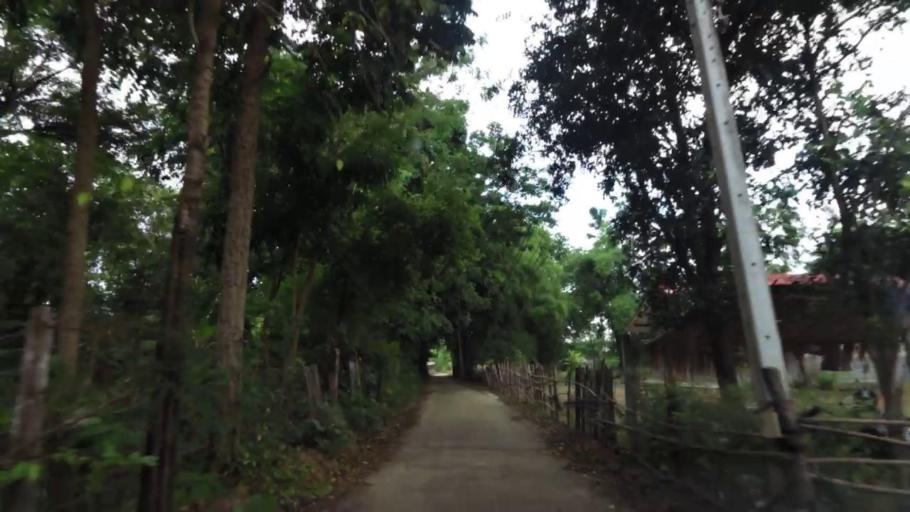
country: TH
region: Nakhon Sawan
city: Phai Sali
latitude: 15.6046
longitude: 100.6669
